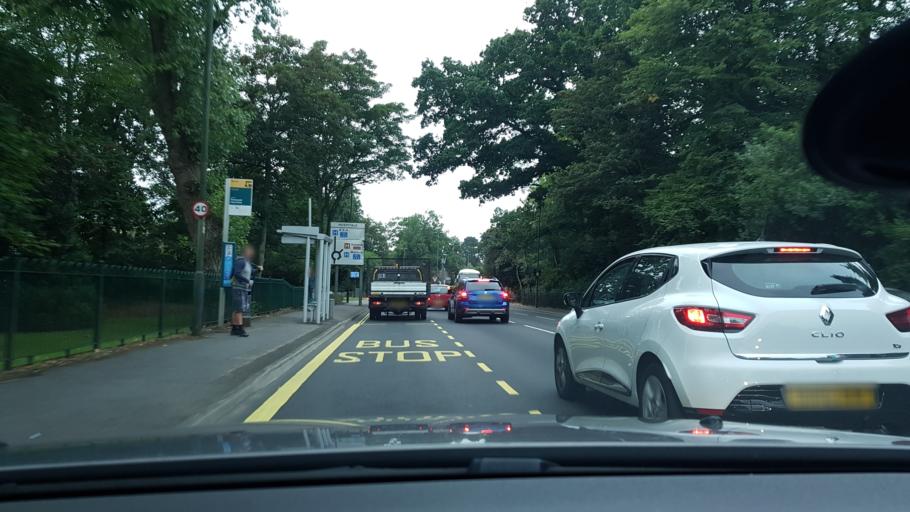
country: GB
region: England
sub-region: Southampton
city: Southampton
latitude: 50.9419
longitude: -1.4065
